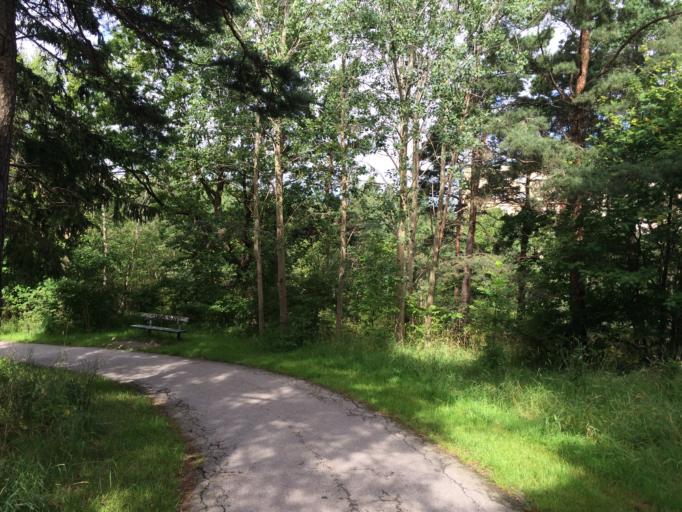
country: SE
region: Stockholm
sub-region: Stockholms Kommun
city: Bromma
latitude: 59.3024
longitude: 17.9848
